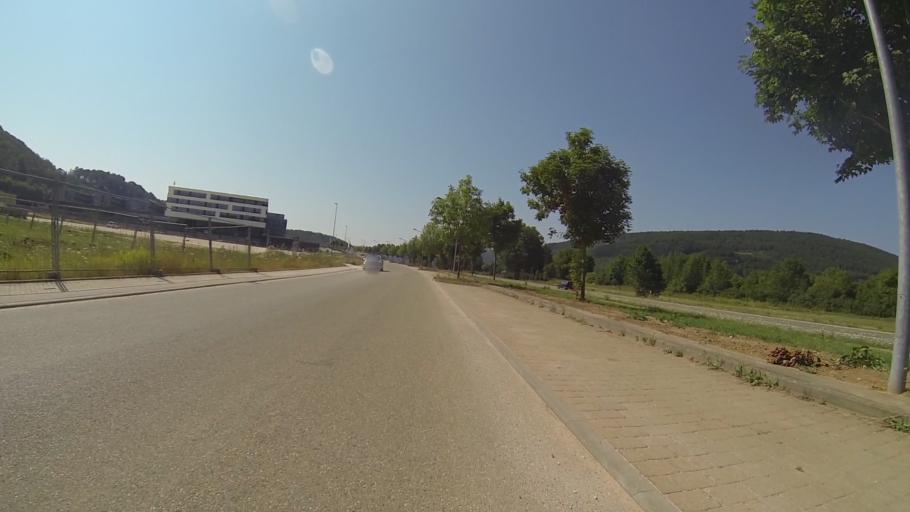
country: DE
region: Baden-Wuerttemberg
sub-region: Regierungsbezirk Stuttgart
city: Oberkochen
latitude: 48.7685
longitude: 10.1013
